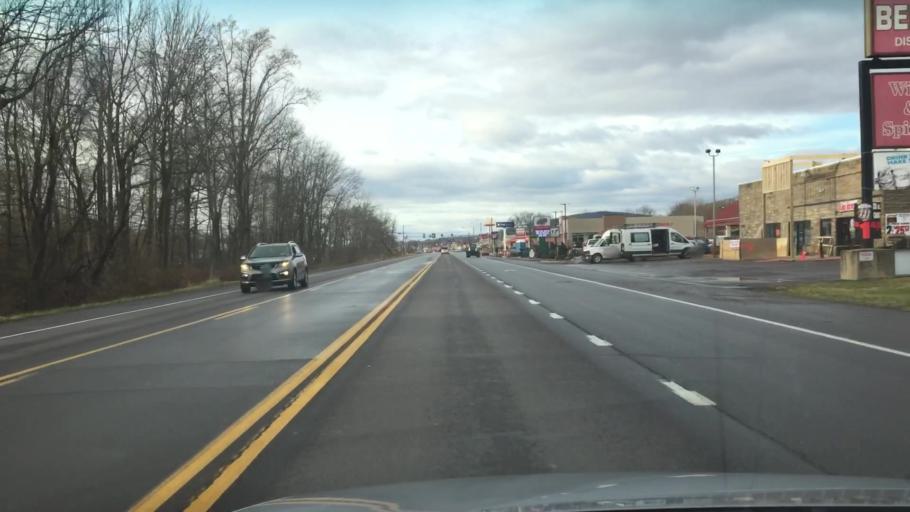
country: US
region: Pennsylvania
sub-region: Columbia County
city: Espy
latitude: 41.0059
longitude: -76.4324
